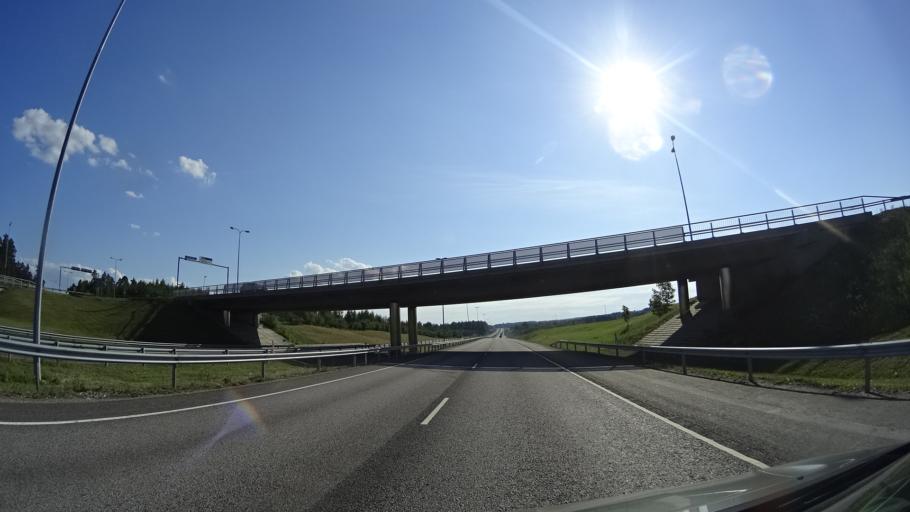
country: FI
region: South Karelia
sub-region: Imatra
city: Imatra
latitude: 61.1848
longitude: 28.7422
